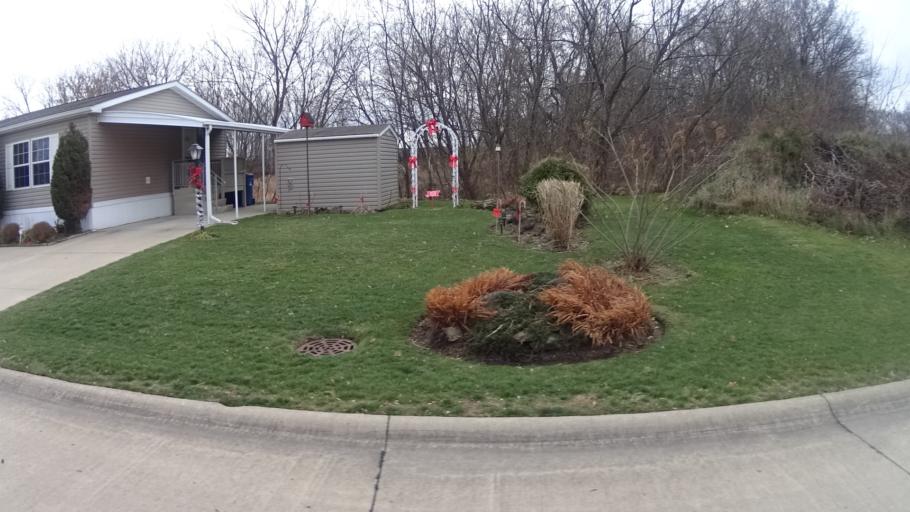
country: US
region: Ohio
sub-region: Lorain County
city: North Ridgeville
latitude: 41.3916
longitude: -82.0071
